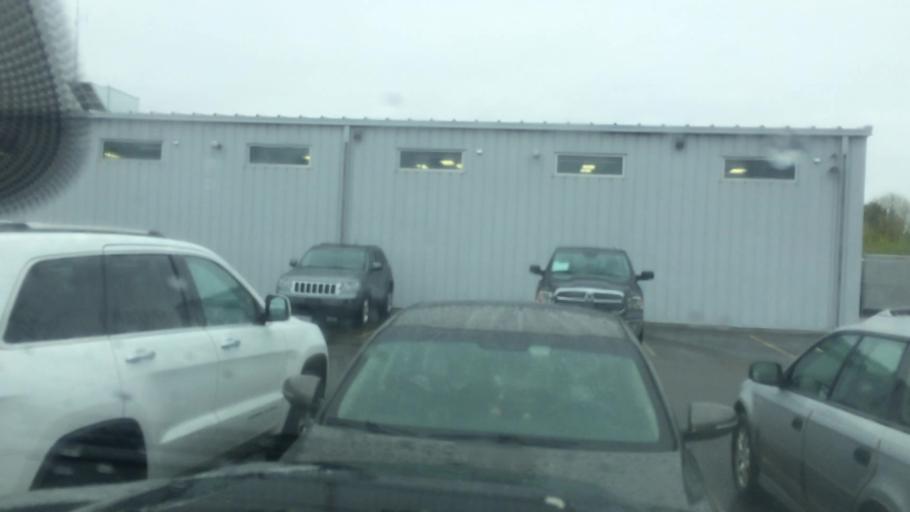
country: US
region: Wisconsin
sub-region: Portage County
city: Whiting
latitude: 44.5223
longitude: -89.5171
